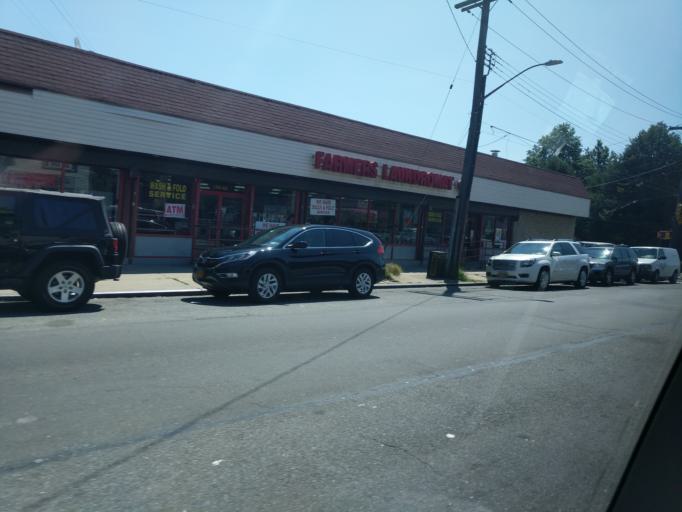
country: US
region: New York
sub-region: Queens County
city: Jamaica
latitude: 40.6741
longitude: -73.7638
